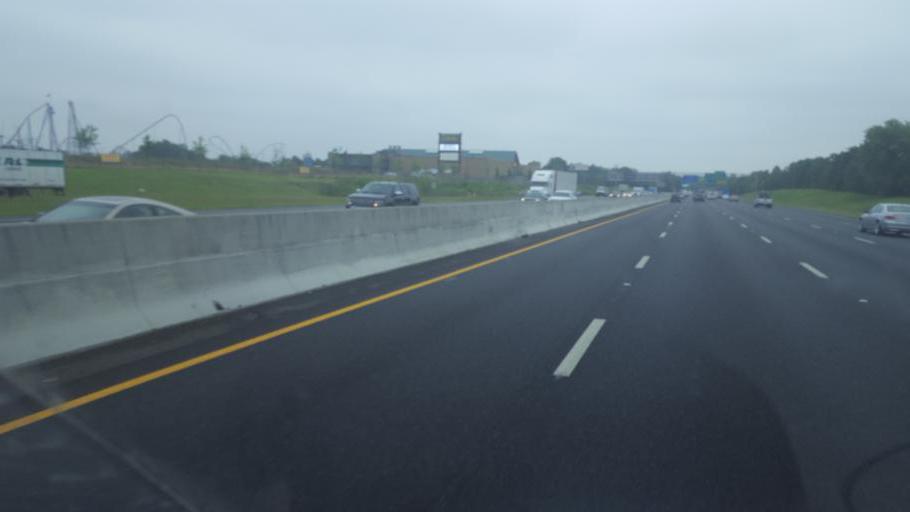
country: US
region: North Carolina
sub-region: Mecklenburg County
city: Pineville
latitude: 35.0964
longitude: -80.9322
